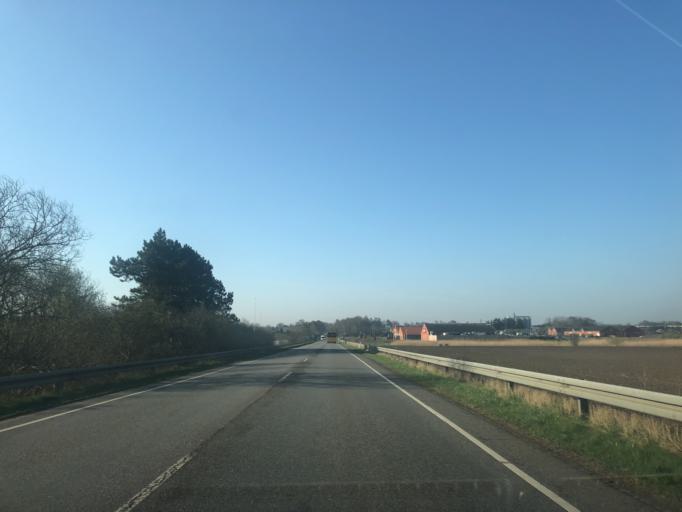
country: DK
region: Zealand
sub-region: Faxe Kommune
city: Haslev
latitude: 55.3338
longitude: 11.9428
